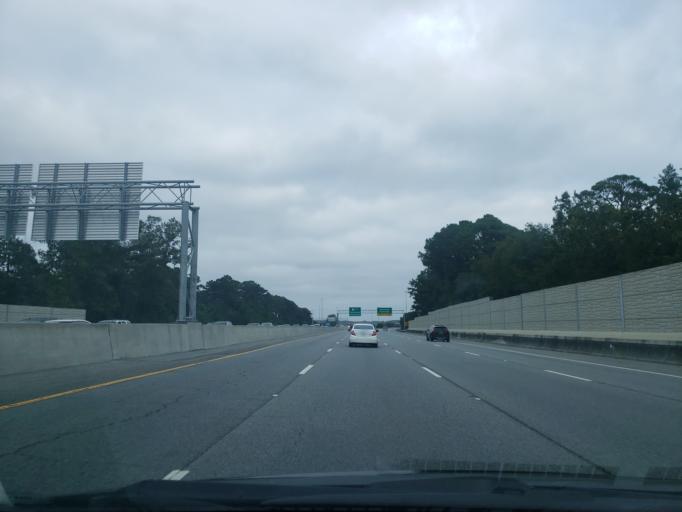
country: US
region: Georgia
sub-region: Chatham County
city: Georgetown
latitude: 31.9837
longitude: -81.2083
